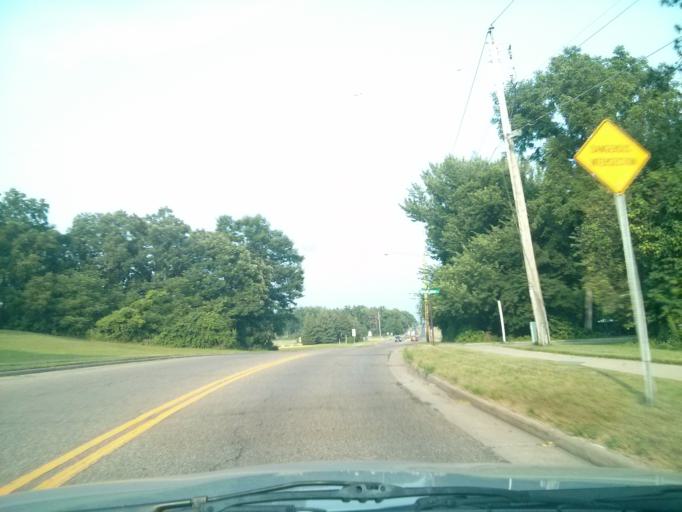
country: US
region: Wisconsin
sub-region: Saint Croix County
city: Hudson
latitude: 44.9776
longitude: -92.7412
